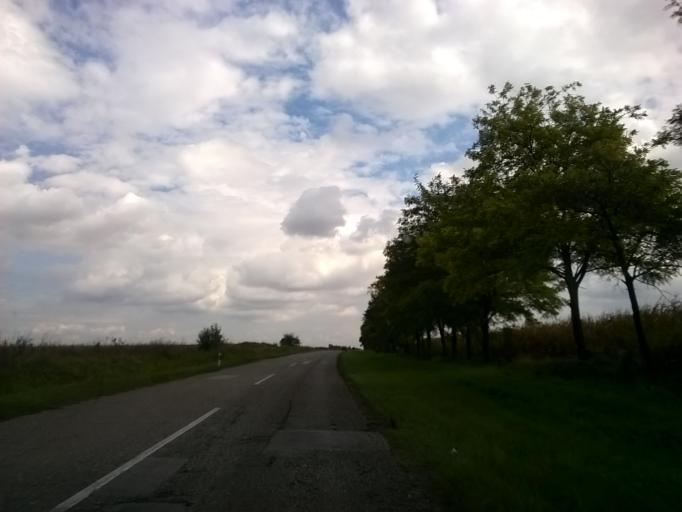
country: RS
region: Autonomna Pokrajina Vojvodina
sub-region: Juznobanatski Okrug
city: Kovacica
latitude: 45.1151
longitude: 20.6634
